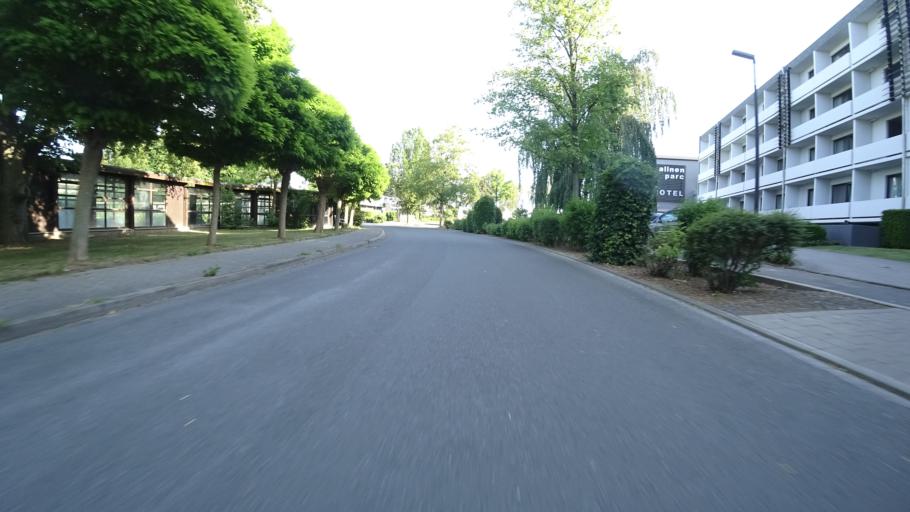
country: DE
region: North Rhine-Westphalia
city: Erwitte
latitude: 51.6306
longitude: 8.3538
